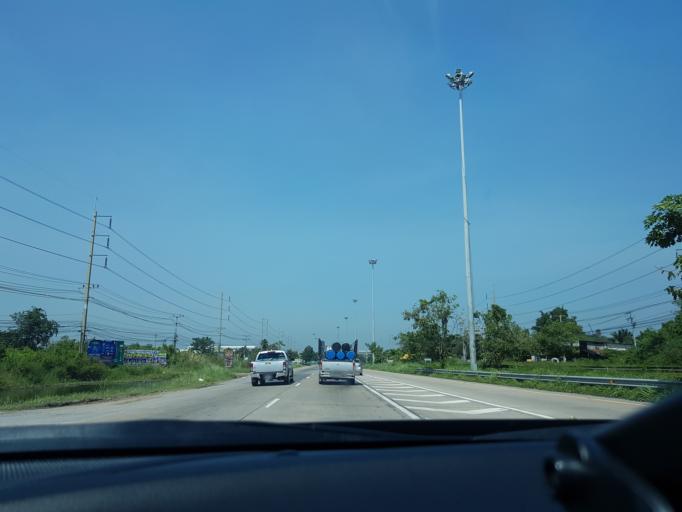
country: TH
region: Sara Buri
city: Saraburi
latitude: 14.5038
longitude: 100.9134
